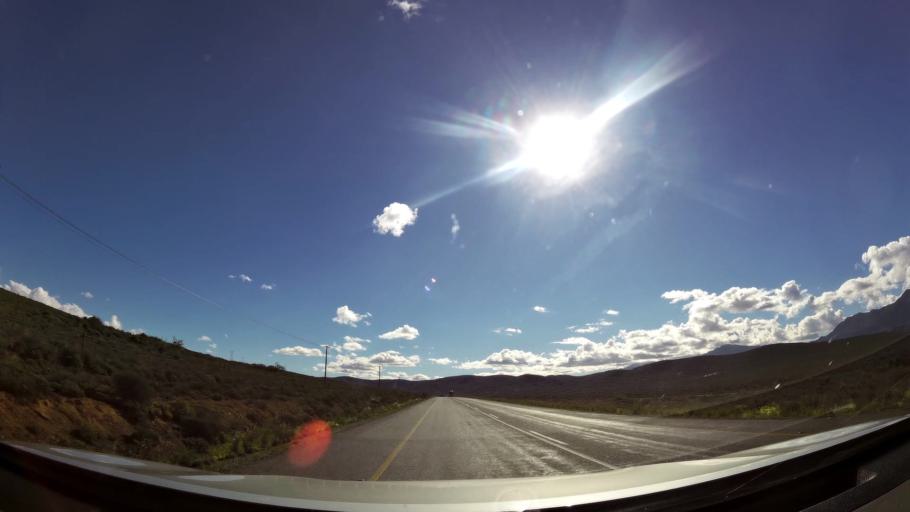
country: ZA
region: Western Cape
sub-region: Cape Winelands District Municipality
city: Worcester
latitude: -33.7442
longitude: 19.6984
